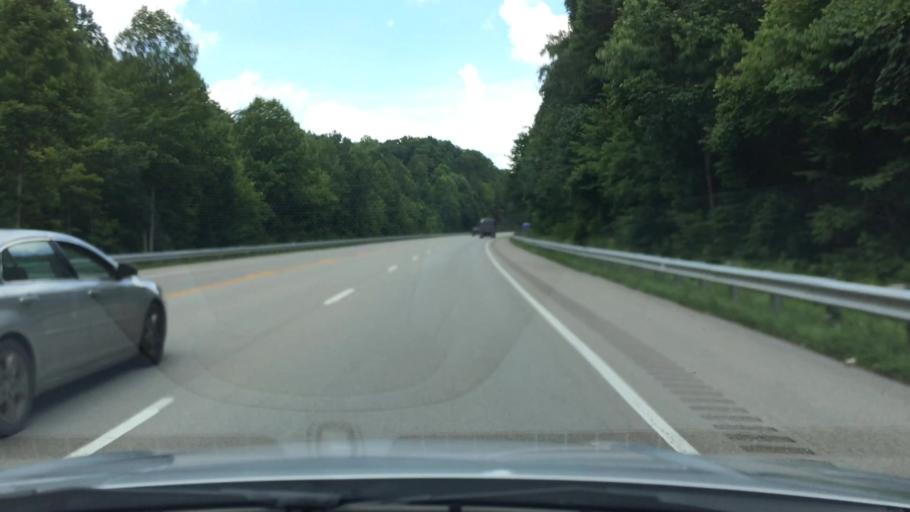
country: US
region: Kentucky
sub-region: McCreary County
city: Whitley City
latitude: 36.9018
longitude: -84.4997
